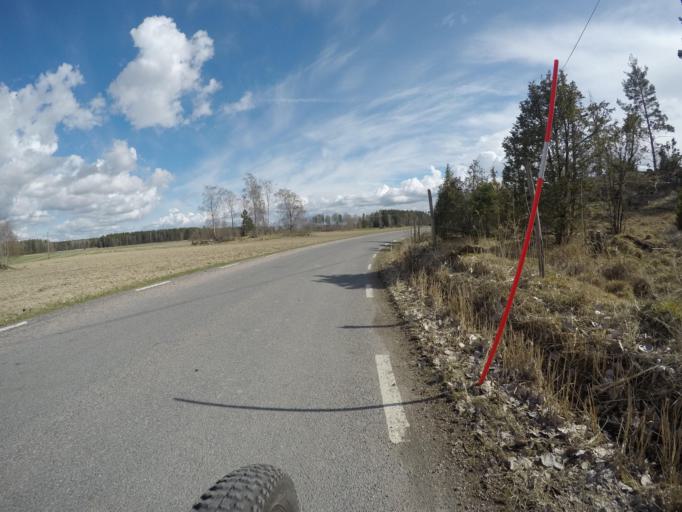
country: SE
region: Vaestmanland
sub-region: Kungsors Kommun
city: Kungsoer
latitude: 59.3077
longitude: 16.1256
